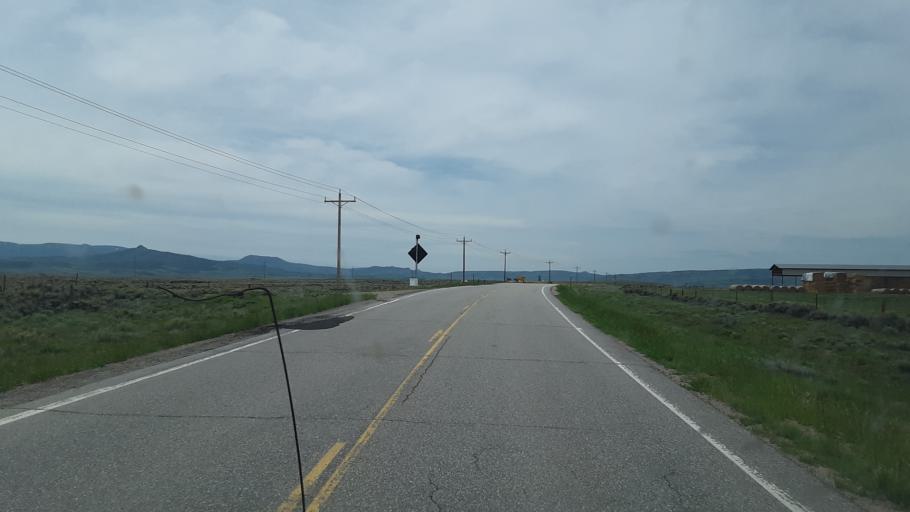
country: US
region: Colorado
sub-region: Jackson County
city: Walden
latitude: 40.5368
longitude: -106.3987
